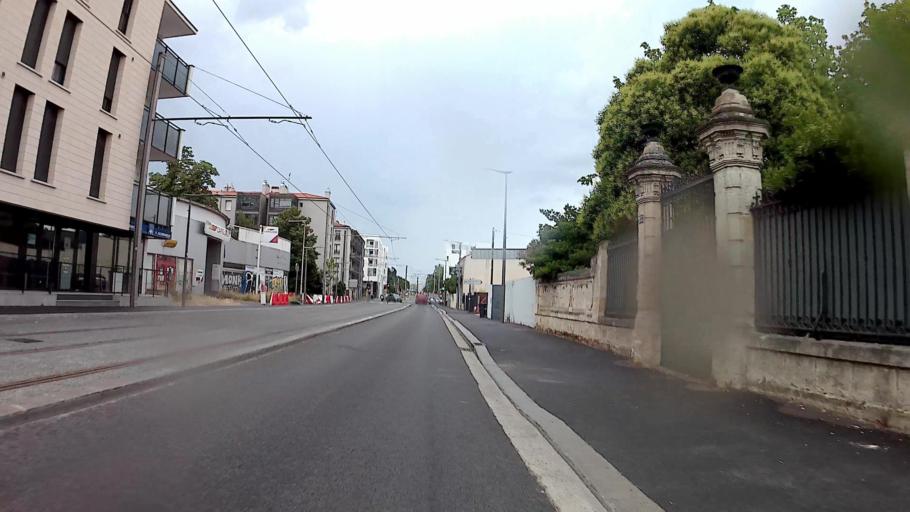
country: FR
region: Aquitaine
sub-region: Departement de la Gironde
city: Le Bouscat
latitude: 44.8639
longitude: -0.6036
